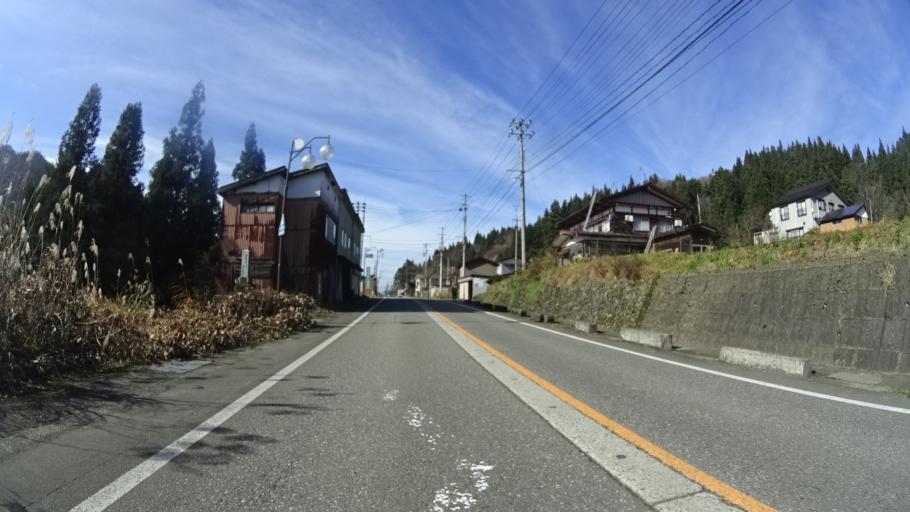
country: JP
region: Niigata
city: Muikamachi
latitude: 37.2068
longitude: 139.0663
